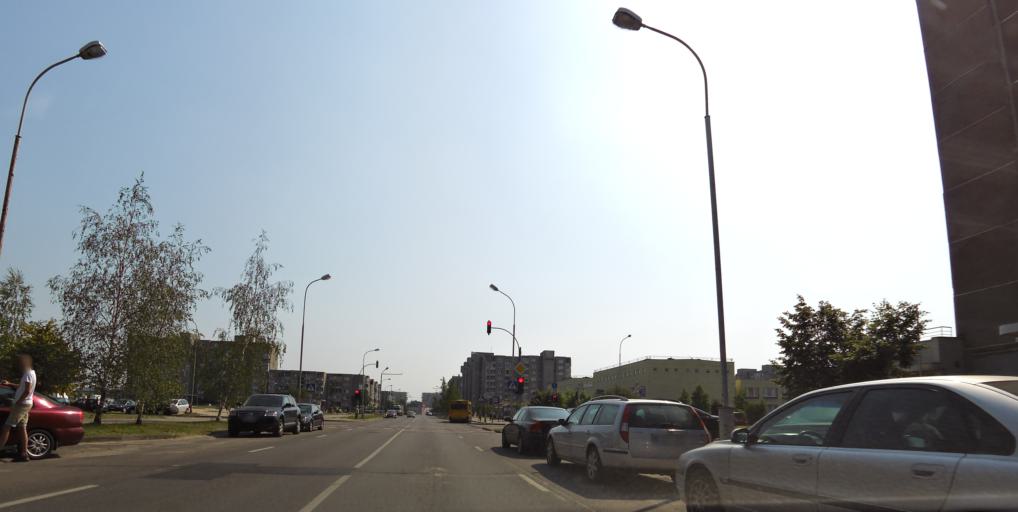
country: LT
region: Vilnius County
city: Pilaite
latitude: 54.7073
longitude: 25.1788
